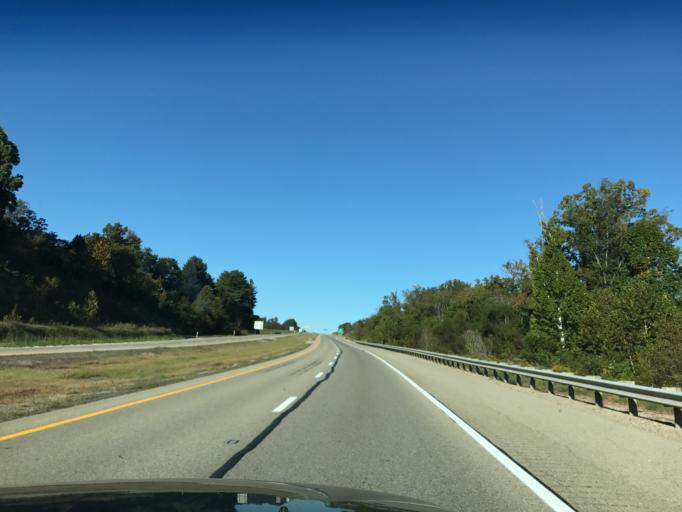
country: US
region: West Virginia
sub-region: Wood County
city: Blennerhassett
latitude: 39.2567
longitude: -81.6246
